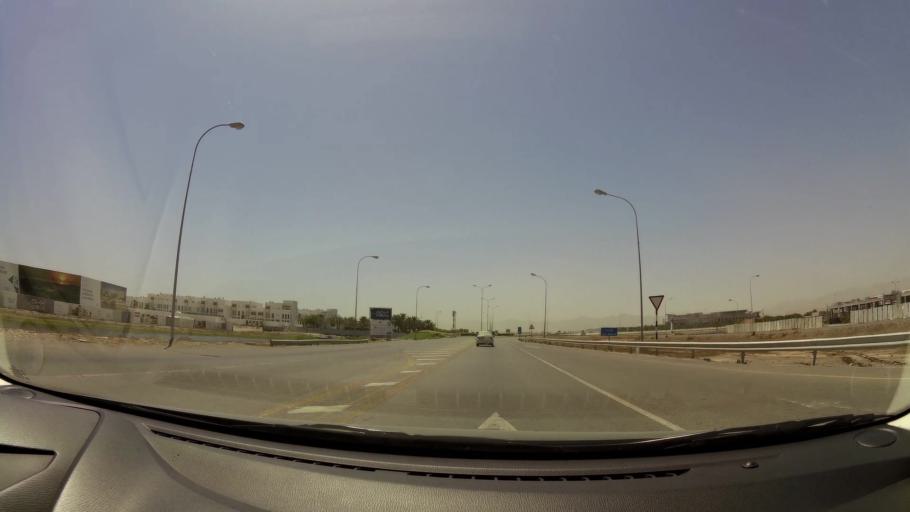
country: OM
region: Muhafazat Masqat
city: As Sib al Jadidah
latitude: 23.6263
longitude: 58.2620
